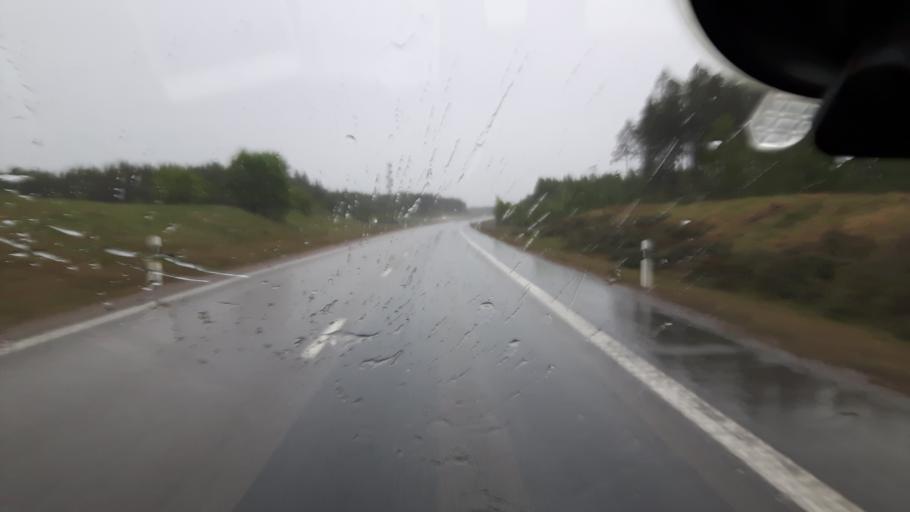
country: SE
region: Uppsala
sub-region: Tierps Kommun
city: Tierp
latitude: 60.2875
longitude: 17.5070
